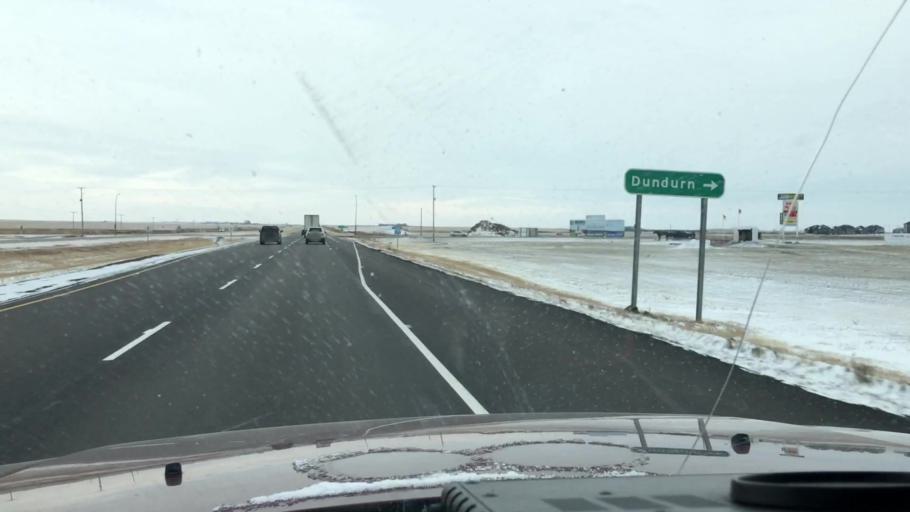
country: CA
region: Saskatchewan
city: Saskatoon
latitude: 51.8108
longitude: -106.4963
